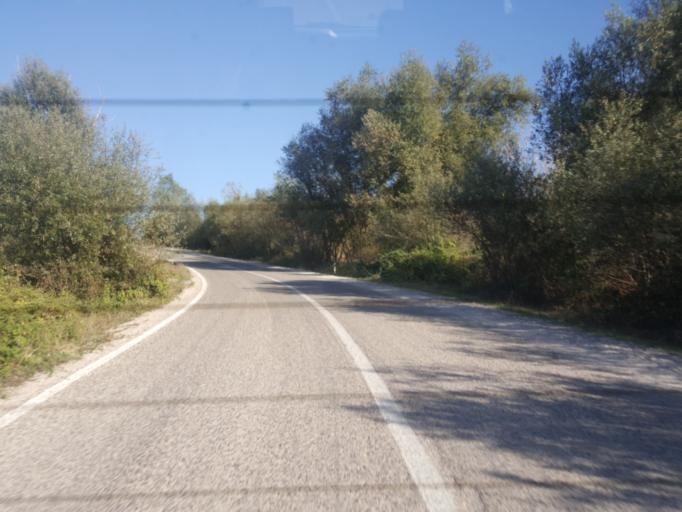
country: TR
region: Amasya
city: Tasova
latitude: 40.7130
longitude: 36.3291
